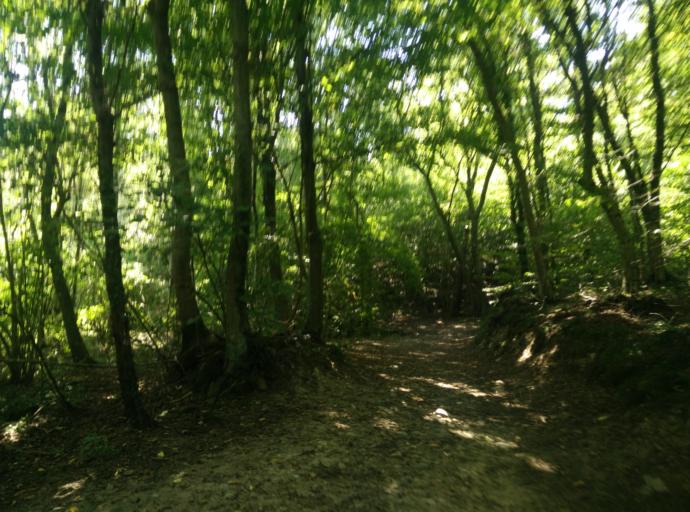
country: IT
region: Piedmont
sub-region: Provincia di Torino
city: Avigliana
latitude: 45.0539
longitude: 7.3843
